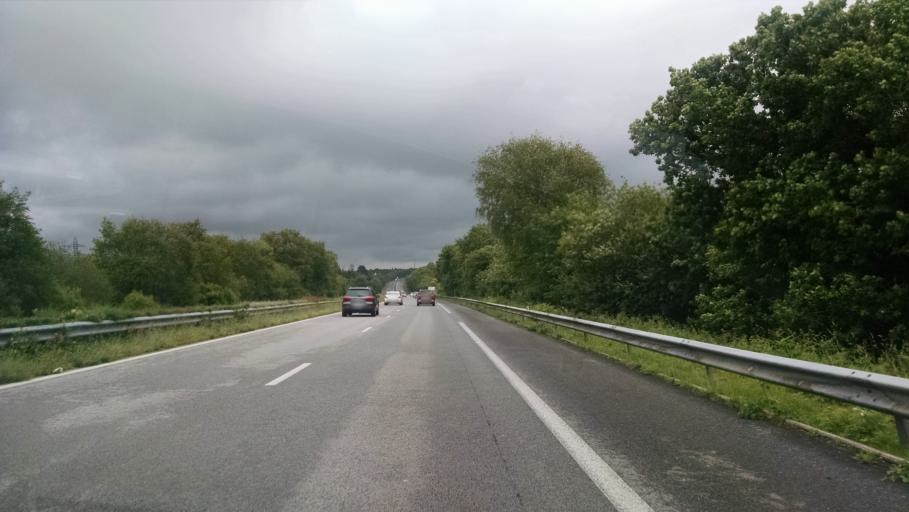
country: FR
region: Brittany
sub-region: Departement du Finistere
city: Melgven
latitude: 47.8977
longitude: -3.8284
